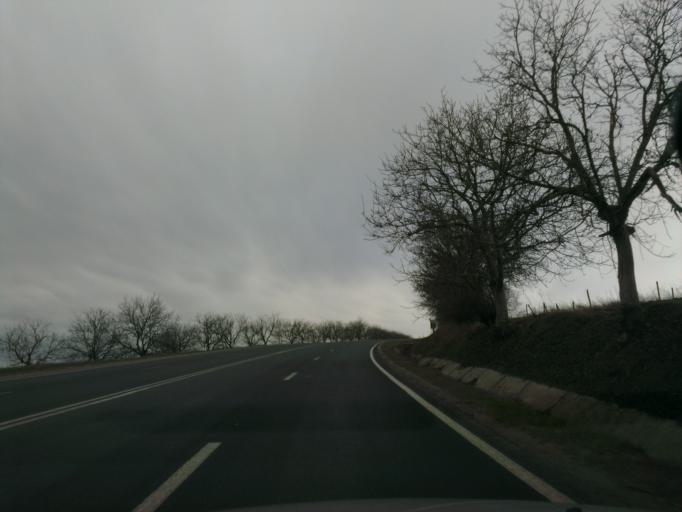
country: MD
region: Laloveni
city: Ialoveni
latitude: 46.9264
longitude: 28.6972
